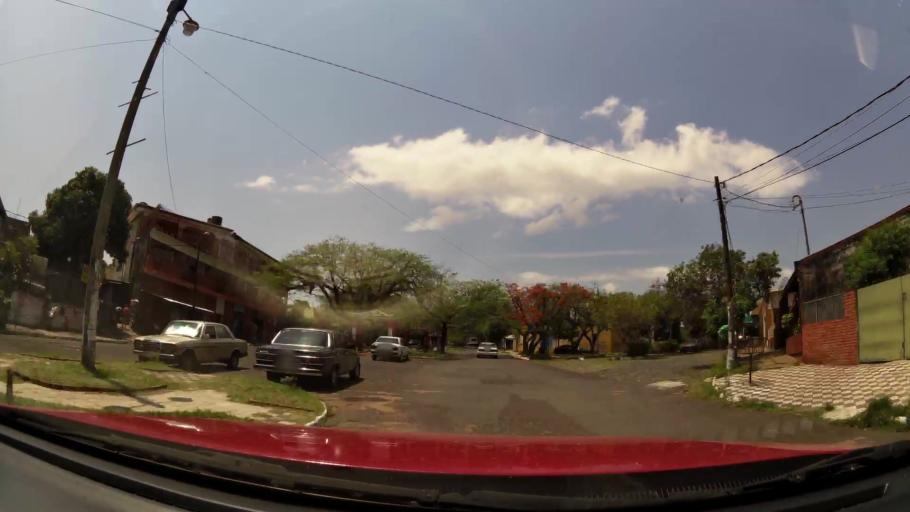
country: PY
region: Asuncion
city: Asuncion
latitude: -25.3003
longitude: -57.6517
